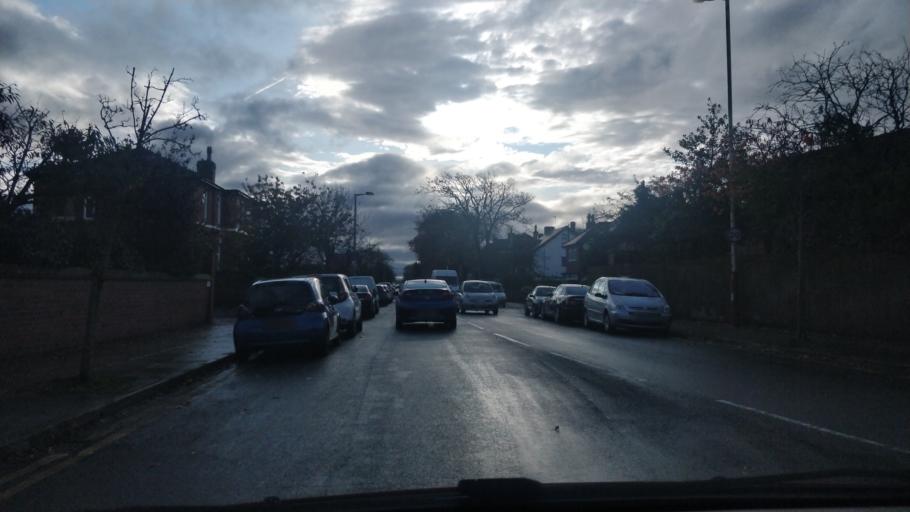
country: GB
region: England
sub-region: Sefton
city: Southport
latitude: 53.6418
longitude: -3.0157
